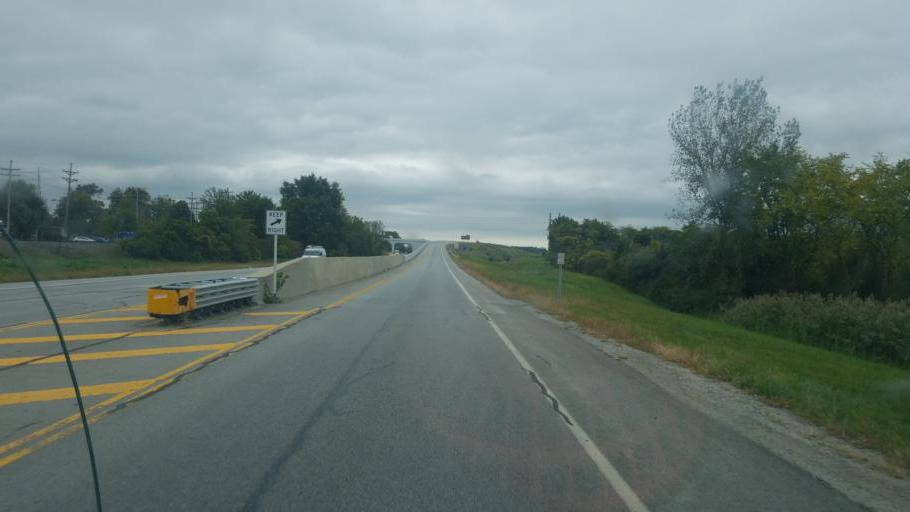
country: US
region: Ohio
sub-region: Lucas County
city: Waterville
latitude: 41.5234
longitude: -83.7173
